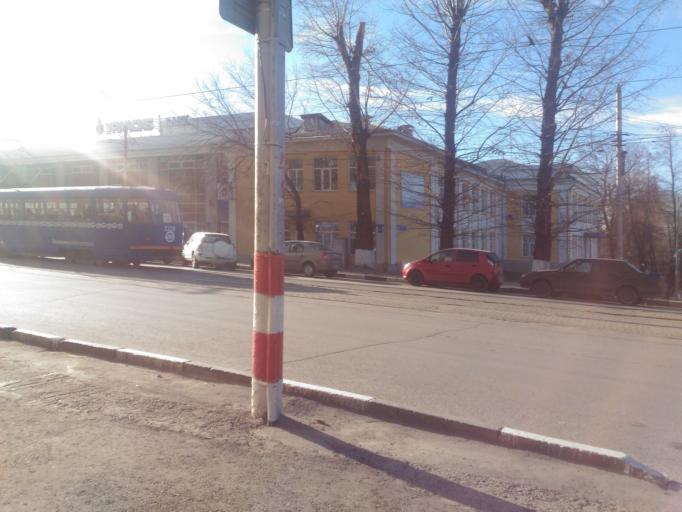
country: RU
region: Ulyanovsk
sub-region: Ulyanovskiy Rayon
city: Ulyanovsk
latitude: 54.3115
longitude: 48.3878
